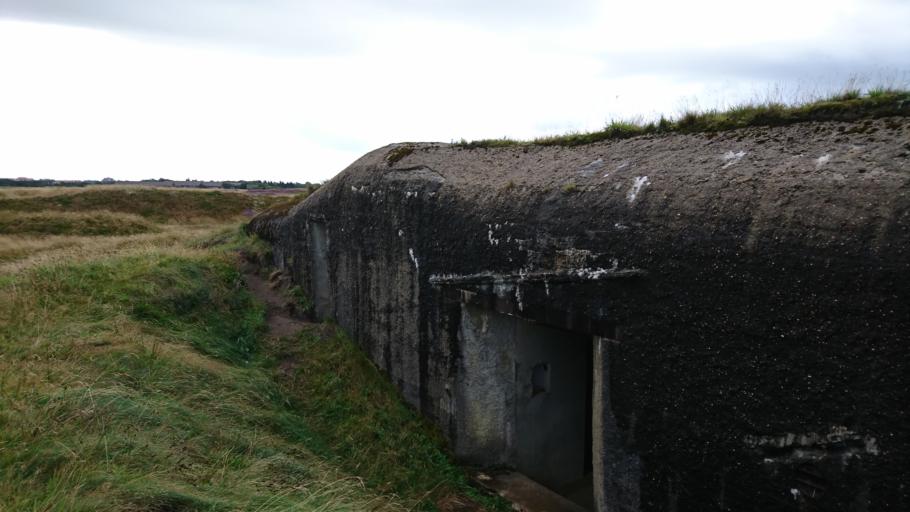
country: DK
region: South Denmark
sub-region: Fano Kommune
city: Nordby
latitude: 55.4607
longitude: 8.3972
